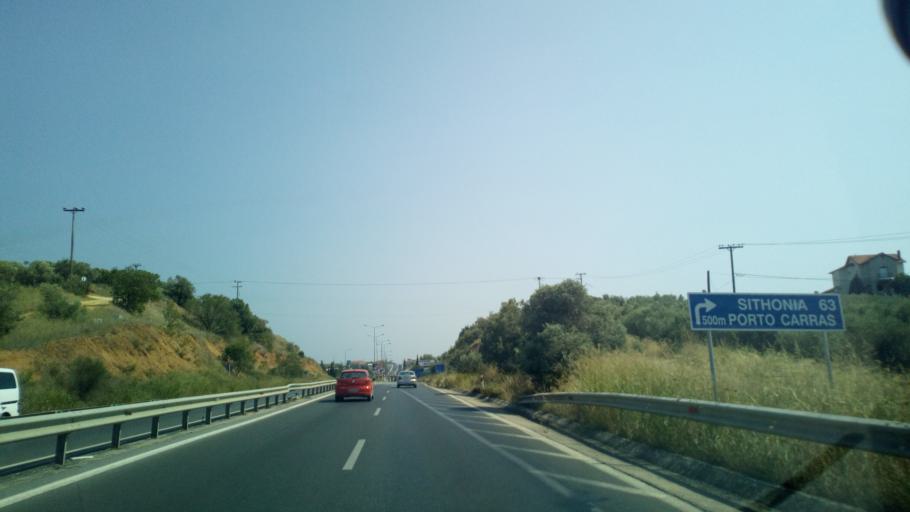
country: GR
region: Central Macedonia
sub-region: Nomos Chalkidikis
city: Nea Moudhania
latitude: 40.2460
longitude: 23.2961
